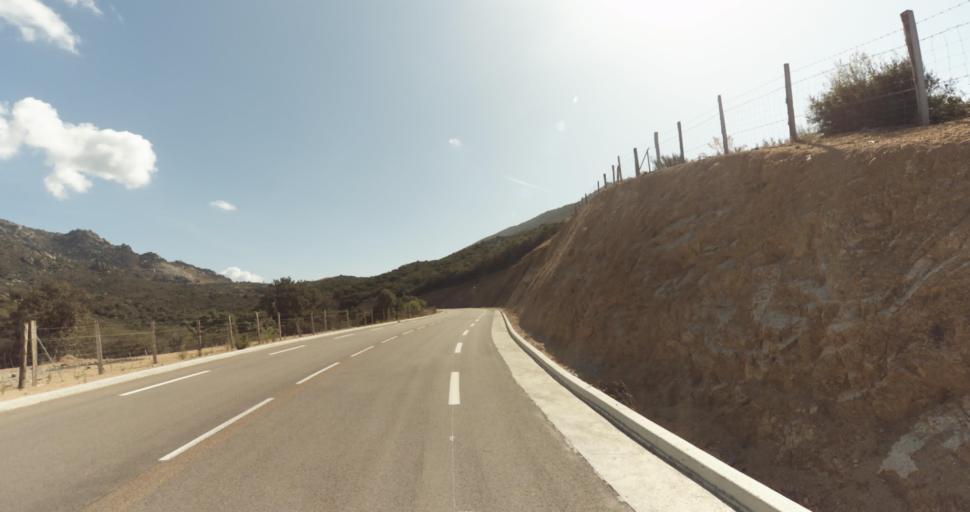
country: FR
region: Corsica
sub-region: Departement de la Corse-du-Sud
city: Ajaccio
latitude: 41.9306
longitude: 8.6543
